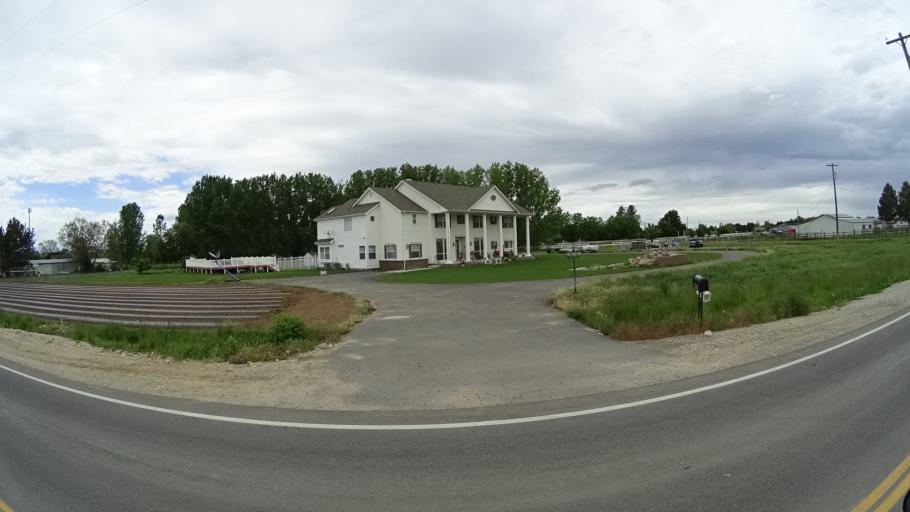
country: US
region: Idaho
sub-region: Ada County
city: Meridian
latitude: 43.5742
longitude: -116.4139
